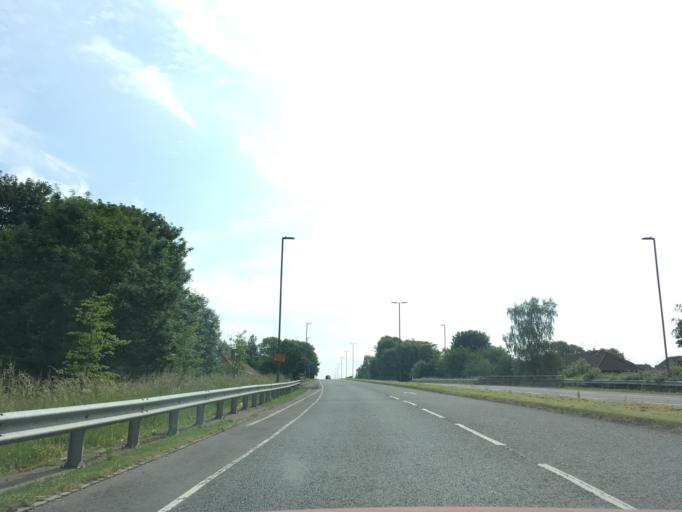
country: GB
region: England
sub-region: South Gloucestershire
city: Chipping Sodbury
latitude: 51.5349
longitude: -2.3996
